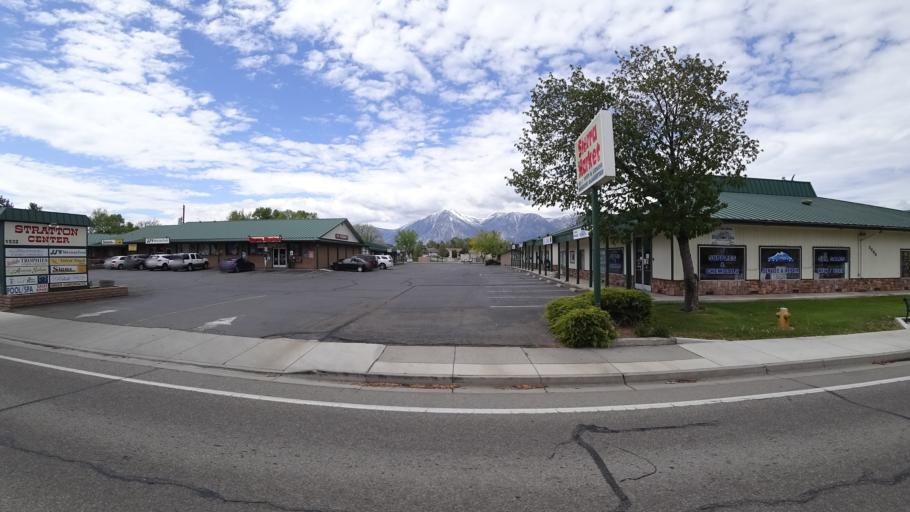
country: US
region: Nevada
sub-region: Douglas County
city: Gardnerville
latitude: 38.9475
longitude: -119.7572
